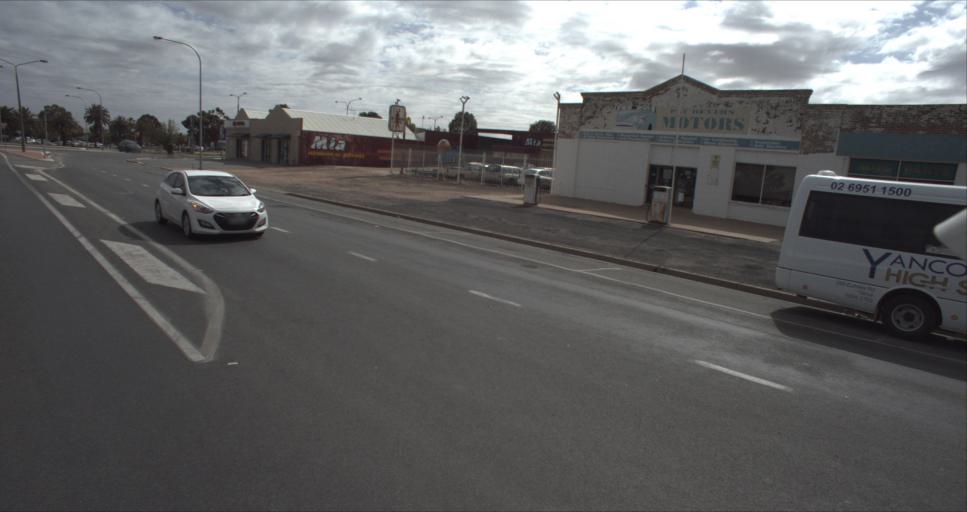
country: AU
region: New South Wales
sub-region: Leeton
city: Leeton
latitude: -34.5525
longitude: 146.3988
